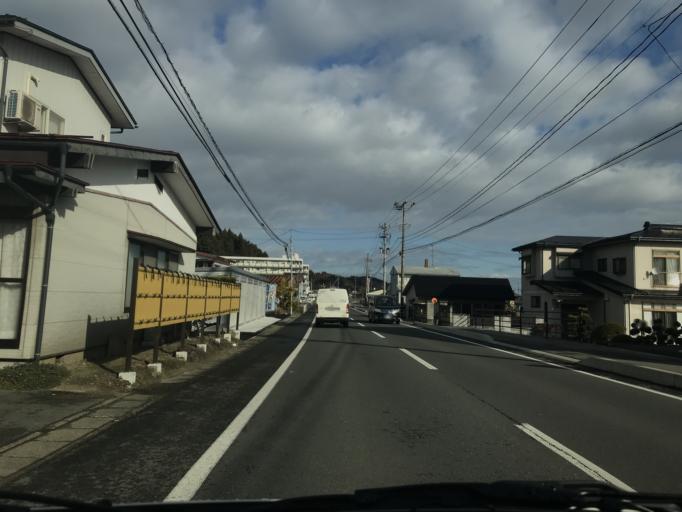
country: JP
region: Iwate
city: Mizusawa
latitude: 39.0618
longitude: 141.1252
